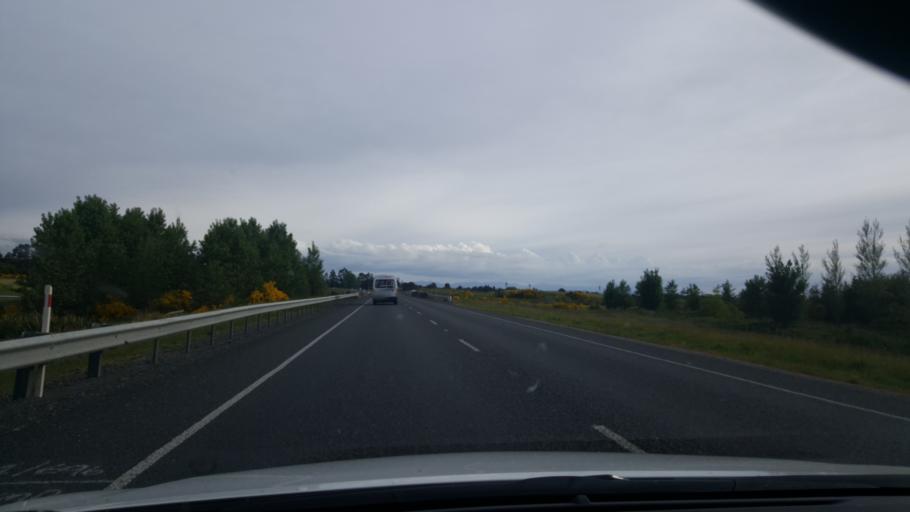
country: NZ
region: Waikato
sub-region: Taupo District
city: Taupo
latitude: -38.6588
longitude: 176.1008
